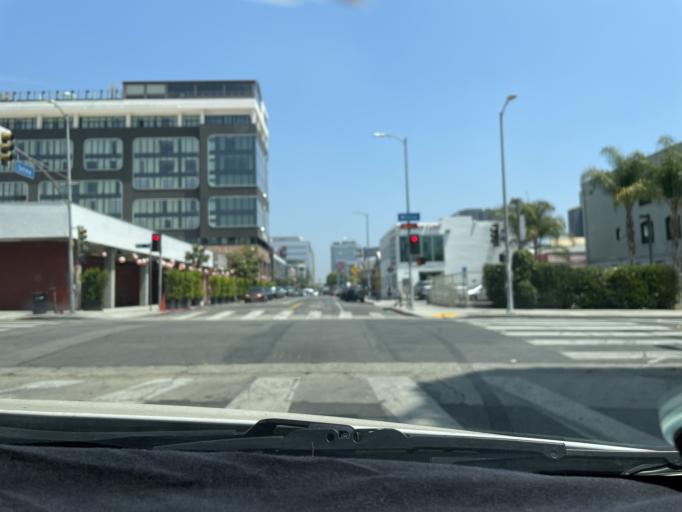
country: US
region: California
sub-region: Los Angeles County
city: Hollywood
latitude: 34.0997
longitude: -118.3312
